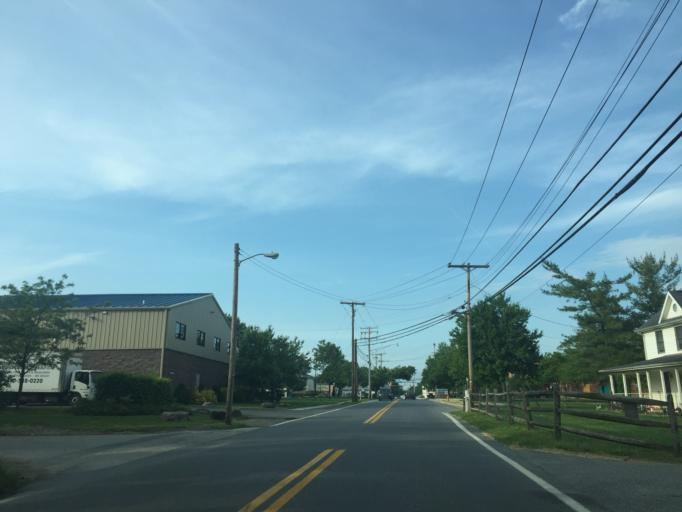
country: US
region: Maryland
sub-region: Baltimore County
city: Edgemere
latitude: 39.2389
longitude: -76.4474
